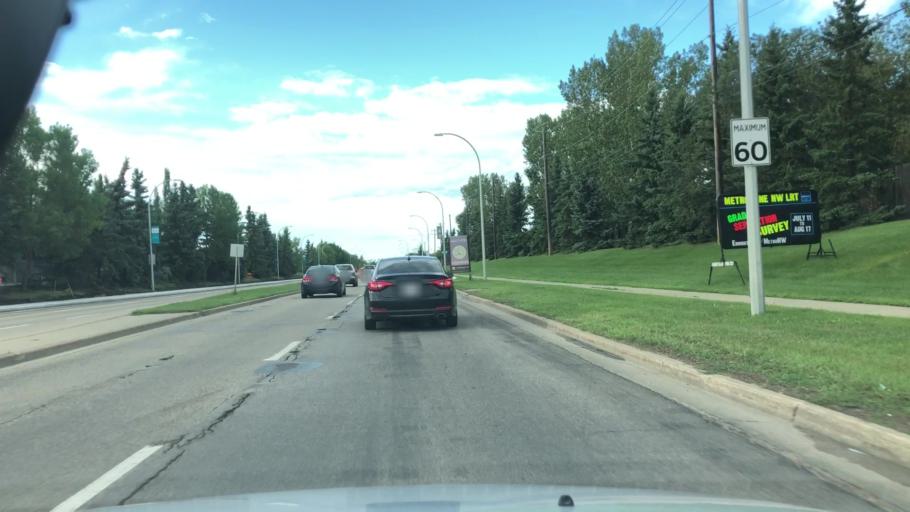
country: CA
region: Alberta
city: St. Albert
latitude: 53.6178
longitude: -113.5411
